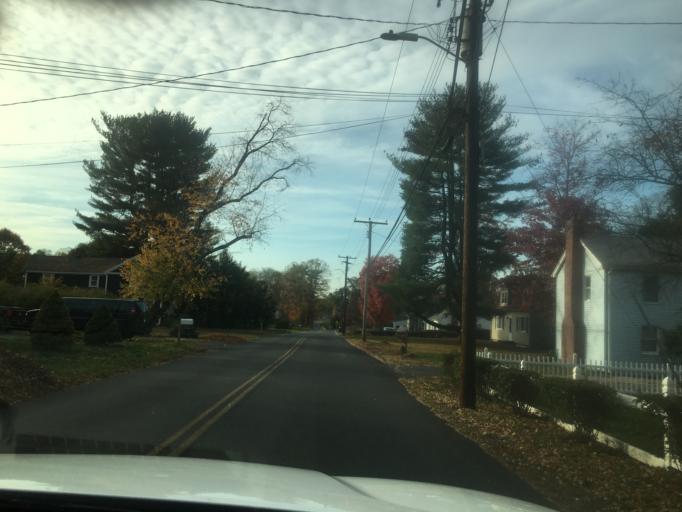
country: US
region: Connecticut
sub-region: Hartford County
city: South Windsor
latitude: 41.8142
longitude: -72.5943
